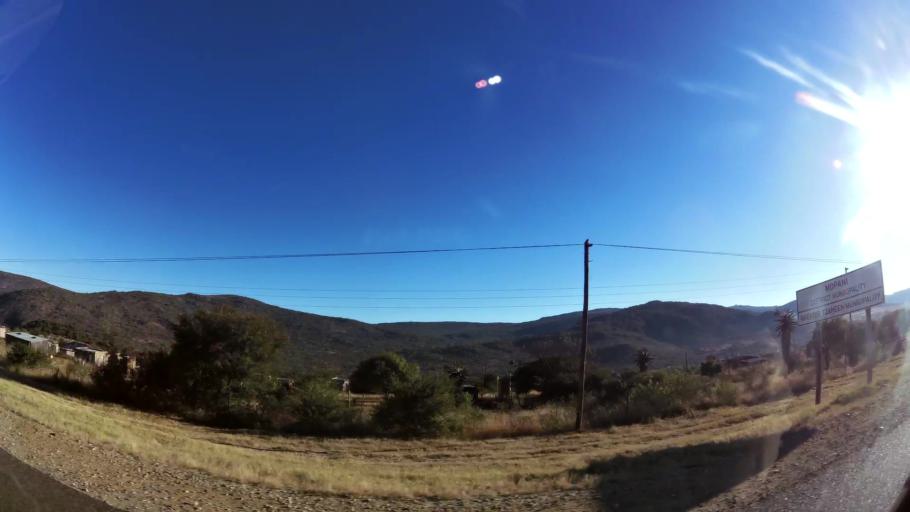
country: ZA
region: Limpopo
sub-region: Capricorn District Municipality
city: Mankoeng
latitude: -23.9293
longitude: 29.8582
